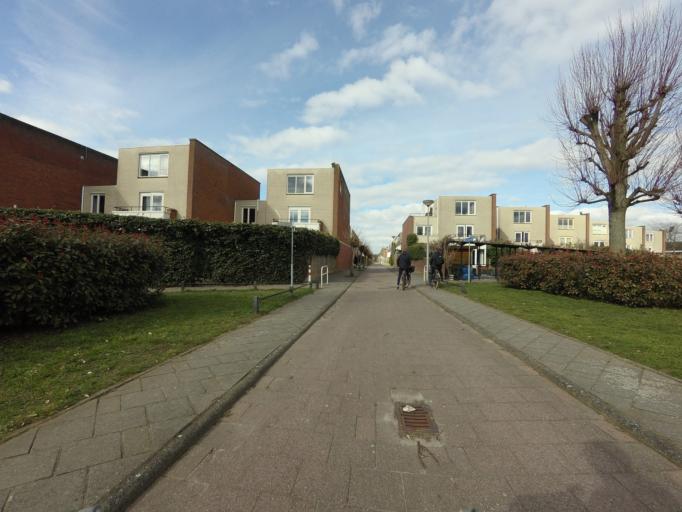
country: NL
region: South Holland
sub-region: Gemeente Alphen aan den Rijn
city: Alphen aan den Rijn
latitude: 52.1174
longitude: 4.6592
